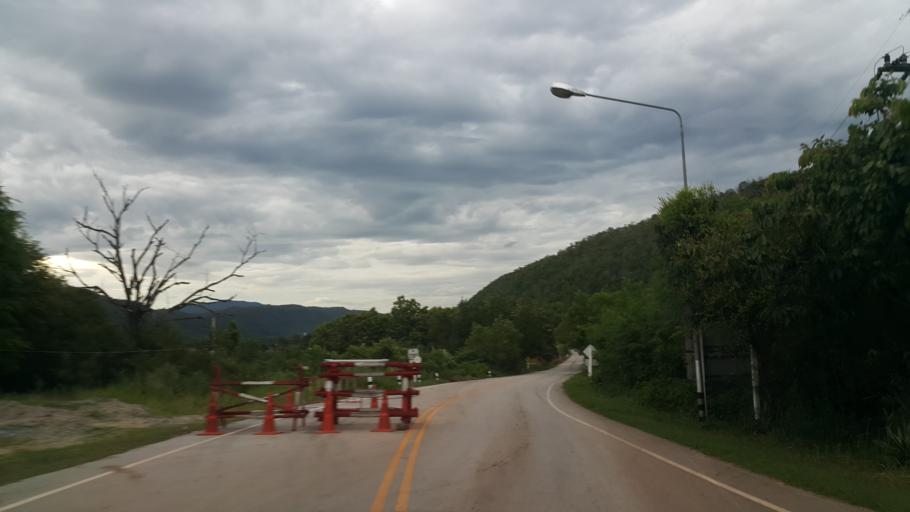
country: TH
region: Loei
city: Na Haeo
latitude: 17.4949
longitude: 101.1846
